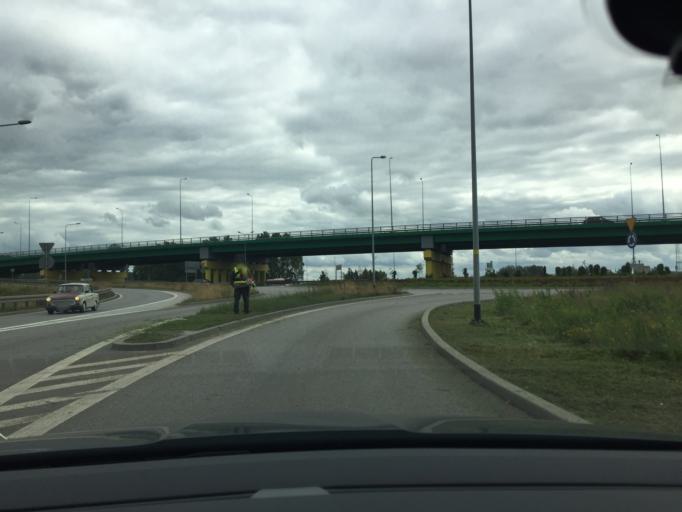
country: PL
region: Pomeranian Voivodeship
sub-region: Gdansk
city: Gdansk
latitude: 54.3791
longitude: 18.6798
